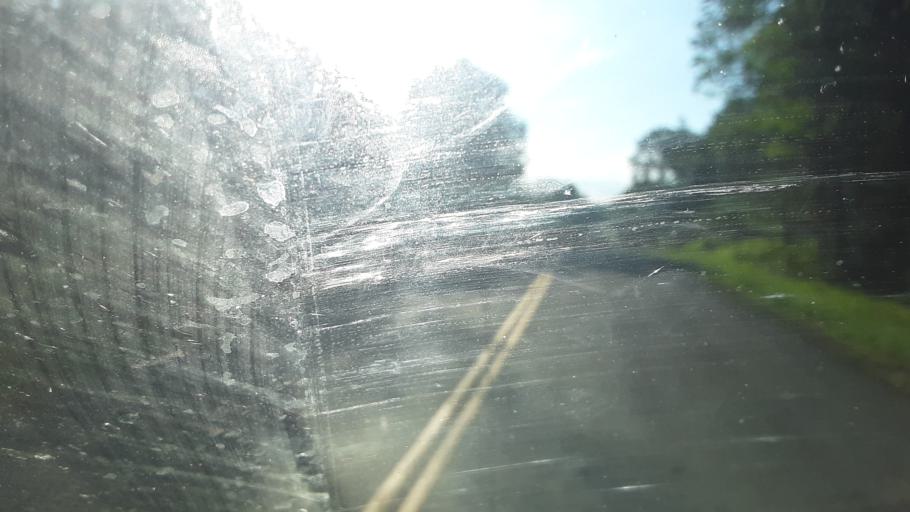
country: US
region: Maine
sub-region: Penobscot County
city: Patten
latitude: 46.2021
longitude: -68.2832
